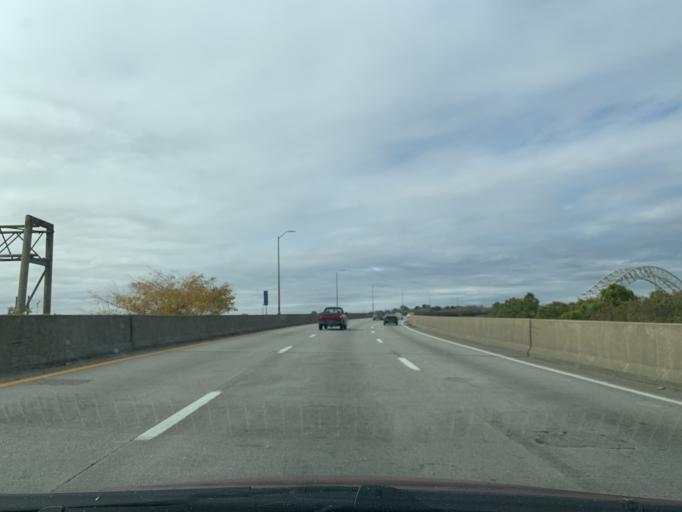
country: US
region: Indiana
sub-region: Floyd County
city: New Albany
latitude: 38.2752
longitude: -85.8151
